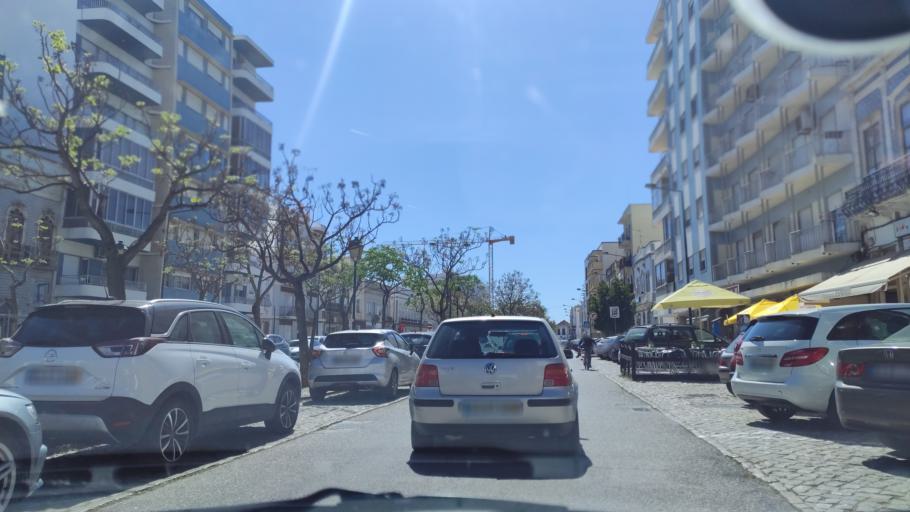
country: PT
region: Faro
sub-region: Olhao
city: Olhao
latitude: 37.0291
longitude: -7.8392
